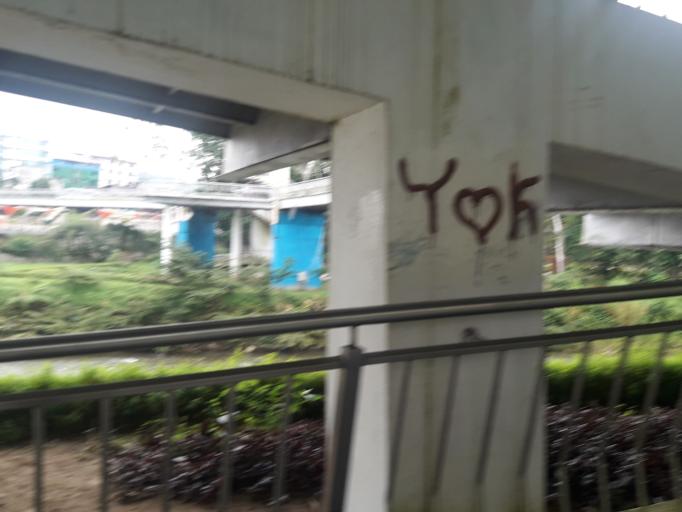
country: EC
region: Napo
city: Tena
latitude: -0.9926
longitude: -77.8160
